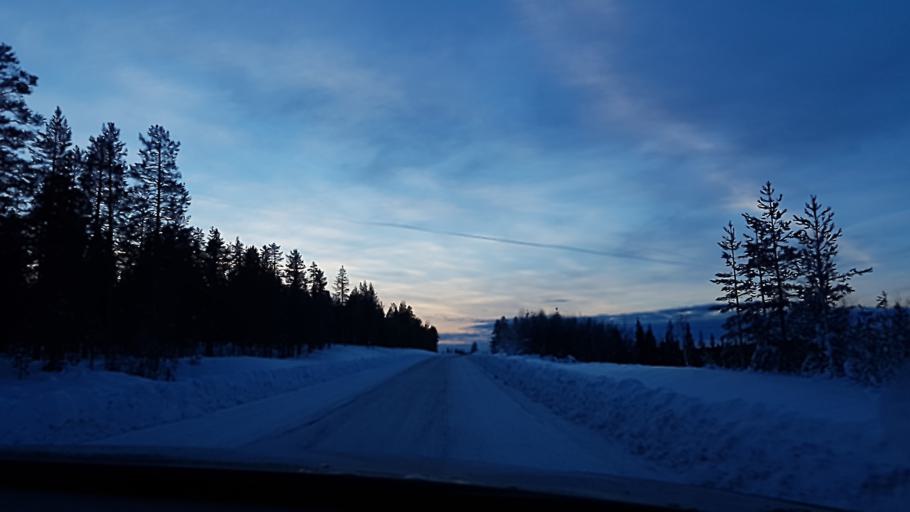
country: SE
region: Norrbotten
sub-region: Jokkmokks Kommun
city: Jokkmokk
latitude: 66.0812
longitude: 20.0737
